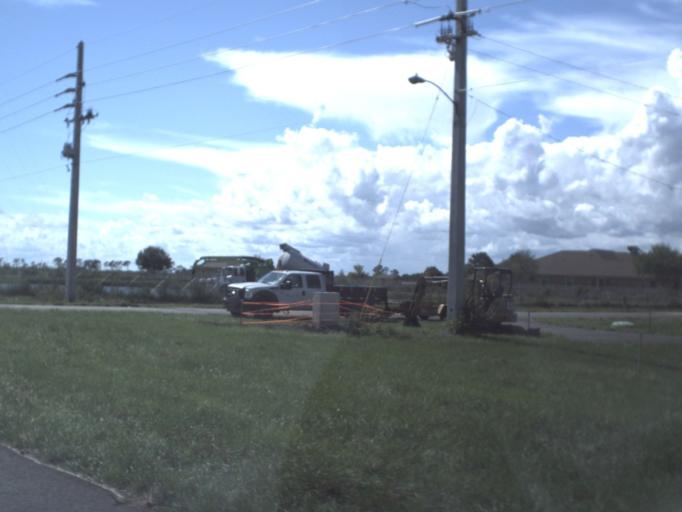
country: US
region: Florida
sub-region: Okeechobee County
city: Taylor Creek
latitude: 27.2877
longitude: -80.7030
